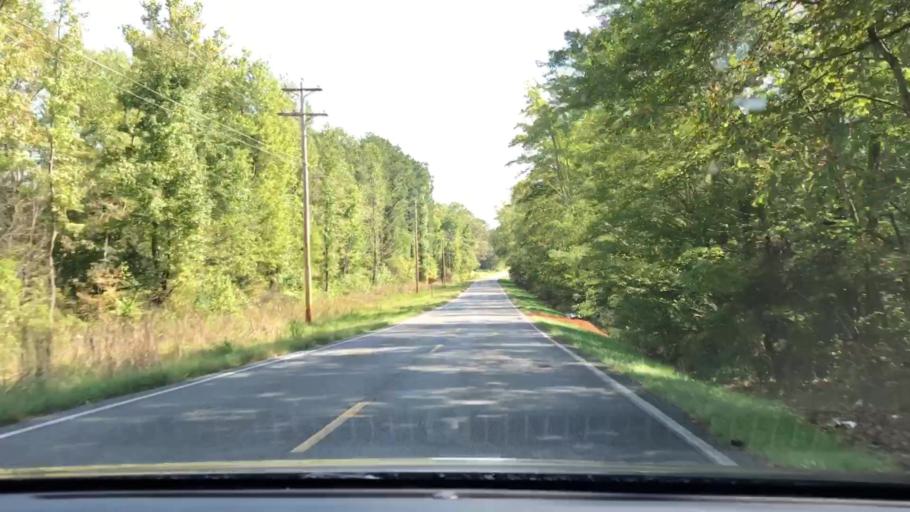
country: US
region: Kentucky
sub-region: Marshall County
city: Benton
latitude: 36.7647
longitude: -88.2489
